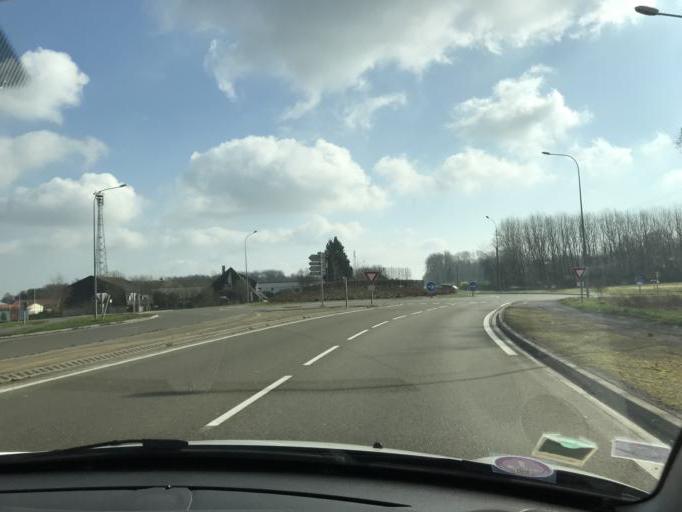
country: FR
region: Picardie
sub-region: Departement de l'Aisne
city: Villeneuve-Saint-Germain
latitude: 49.3687
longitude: 3.3626
